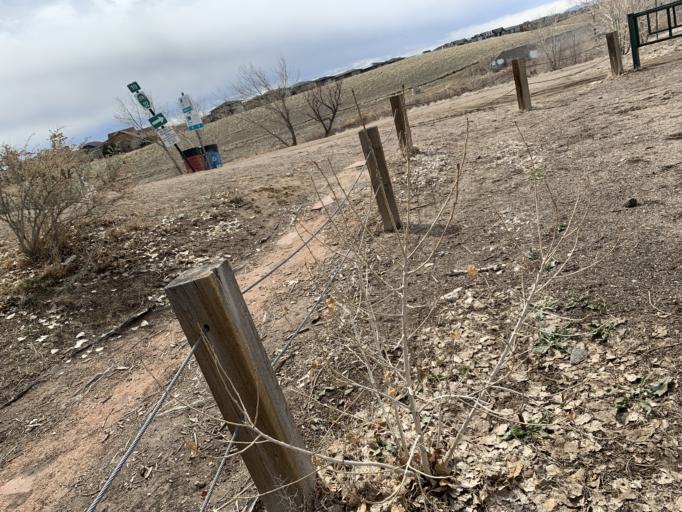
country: US
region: Colorado
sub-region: Adams County
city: Aurora
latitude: 39.7686
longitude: -104.8774
